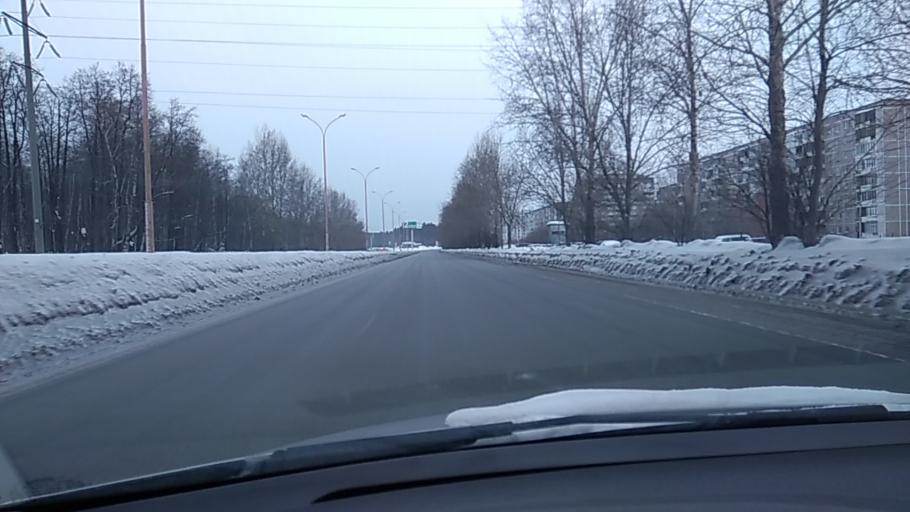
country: RU
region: Sverdlovsk
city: Sovkhoznyy
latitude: 56.7989
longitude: 60.5541
